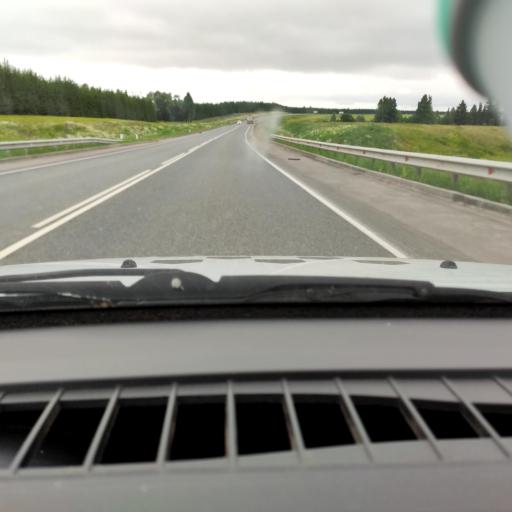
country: RU
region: Udmurtiya
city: Alnashi
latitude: 56.0737
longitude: 52.3979
